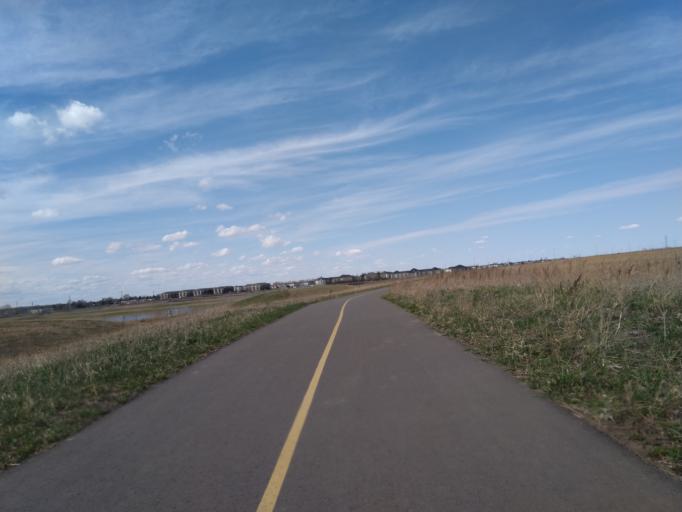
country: CA
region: Alberta
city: Chestermere
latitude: 51.0298
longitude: -113.9236
